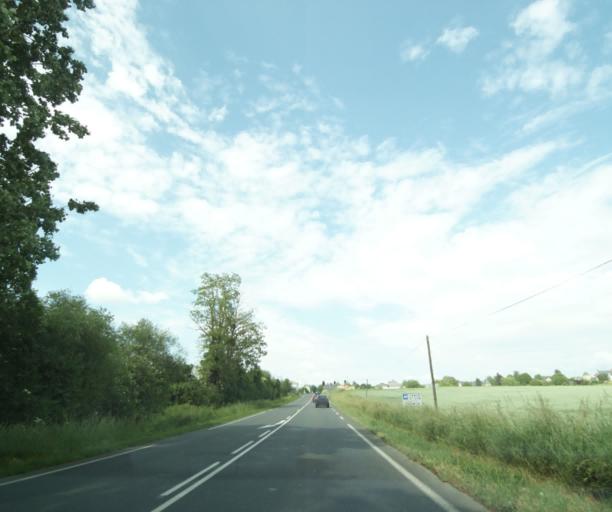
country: FR
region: Pays de la Loire
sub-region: Departement de Maine-et-Loire
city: Distre
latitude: 47.1915
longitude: -0.1276
